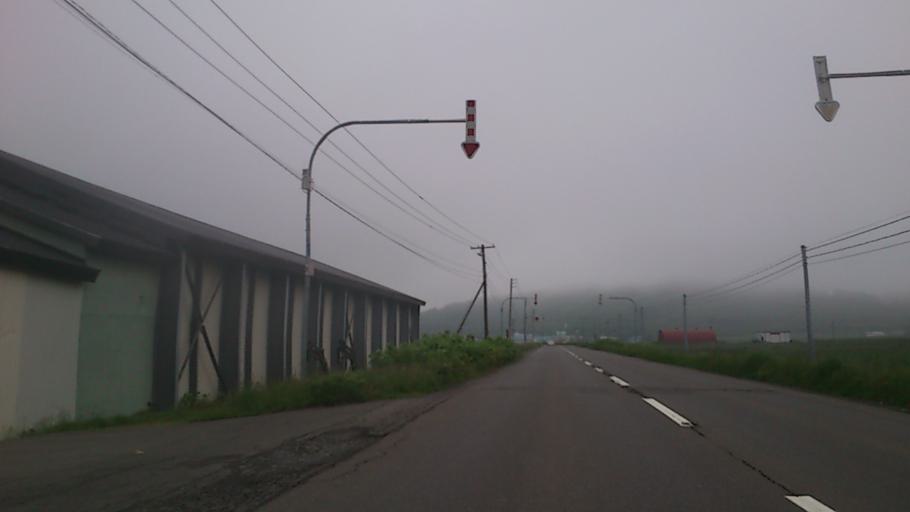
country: JP
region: Hokkaido
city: Niseko Town
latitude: 42.8208
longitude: 140.8904
